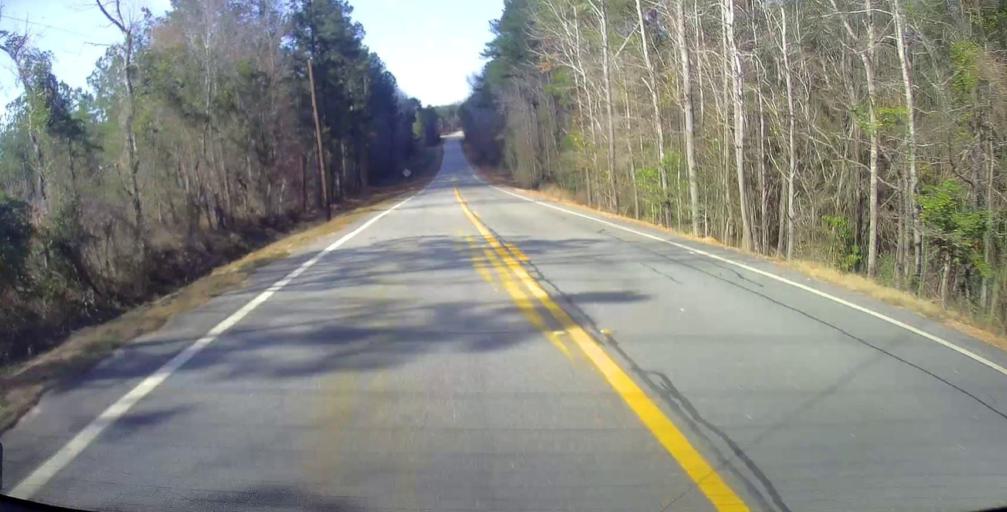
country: US
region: Georgia
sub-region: Wilkinson County
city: Gordon
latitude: 32.8250
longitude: -83.3273
